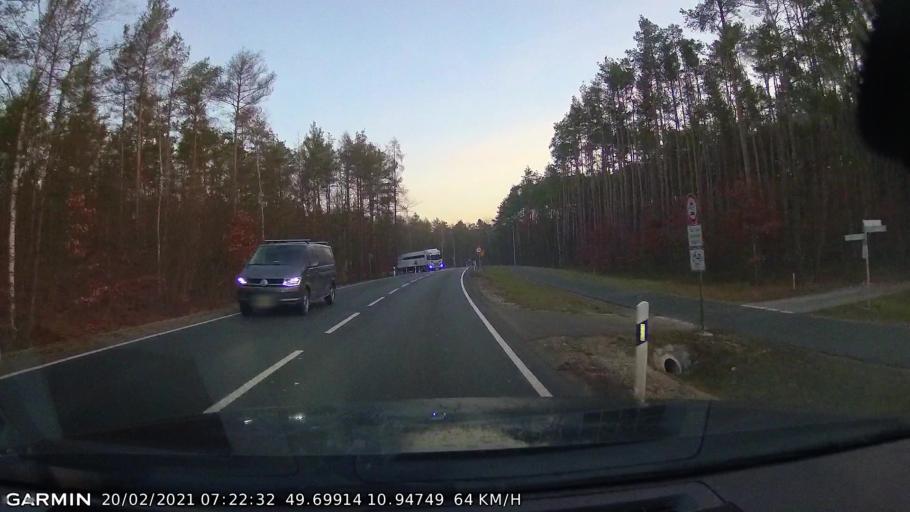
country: DE
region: Bavaria
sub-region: Regierungsbezirk Mittelfranken
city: Hemhofen
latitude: 49.6993
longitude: 10.9475
